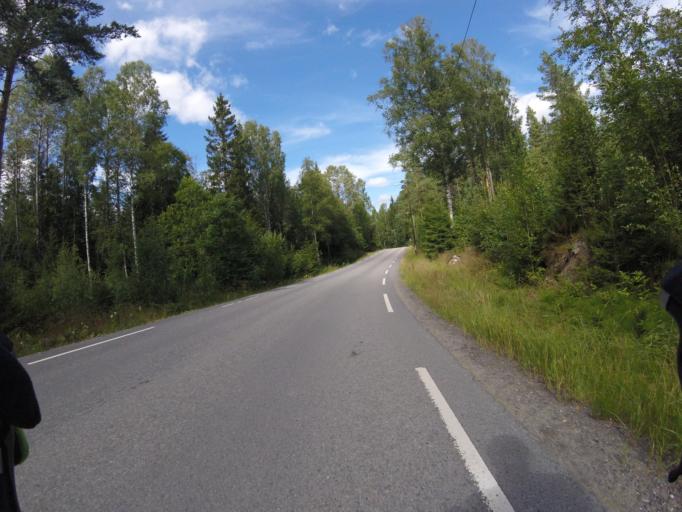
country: NO
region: Akershus
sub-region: Lorenskog
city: Kjenn
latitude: 59.8944
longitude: 10.9749
